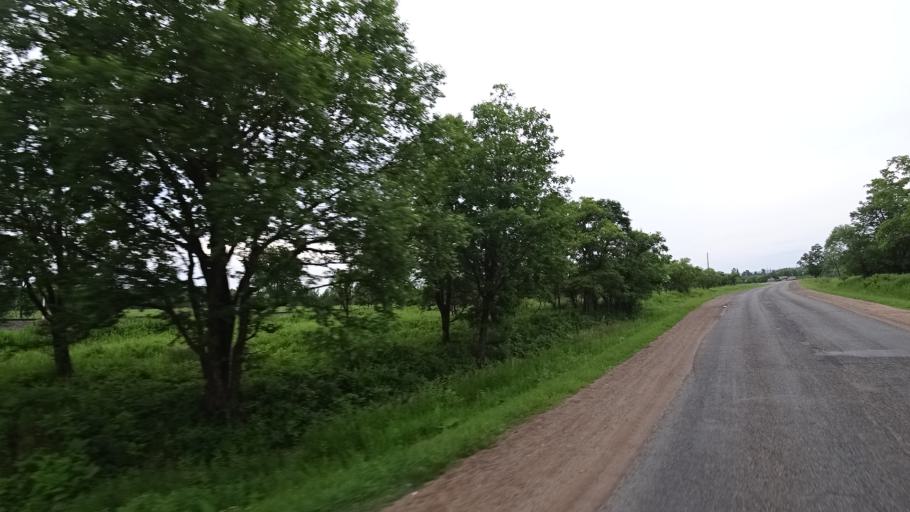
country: RU
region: Primorskiy
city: Novosysoyevka
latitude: 44.2224
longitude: 133.3499
